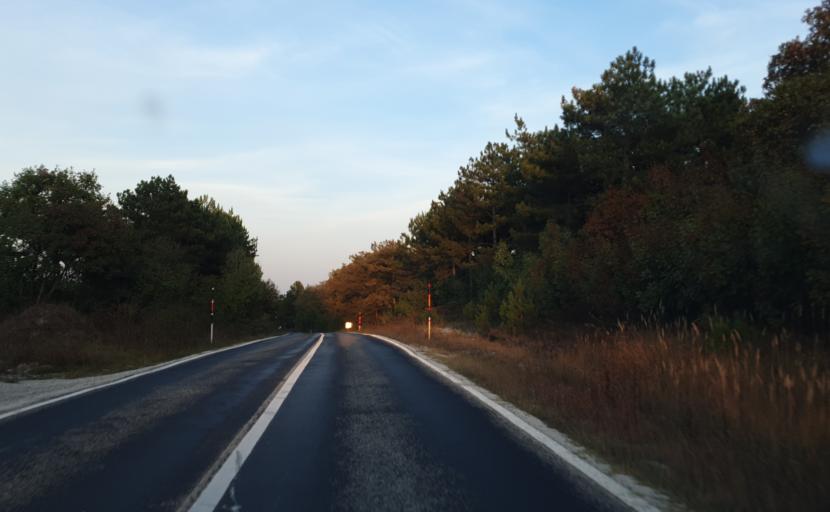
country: TR
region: Kirklareli
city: Igneada
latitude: 41.8609
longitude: 27.8647
